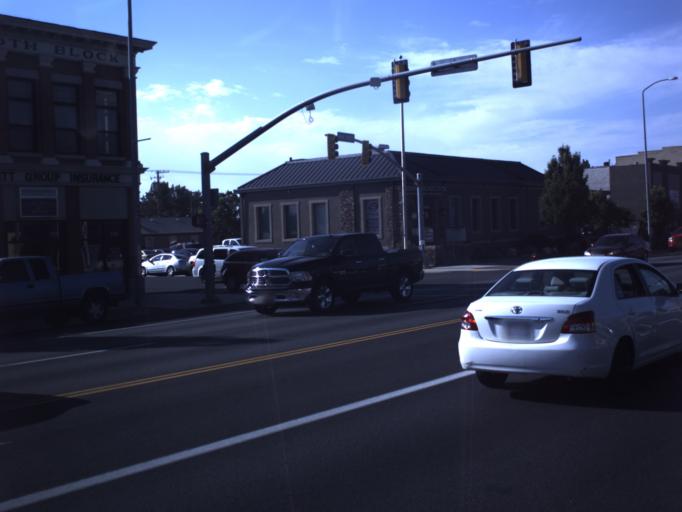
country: US
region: Utah
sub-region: Utah County
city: Spanish Fork
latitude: 40.1122
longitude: -111.6547
